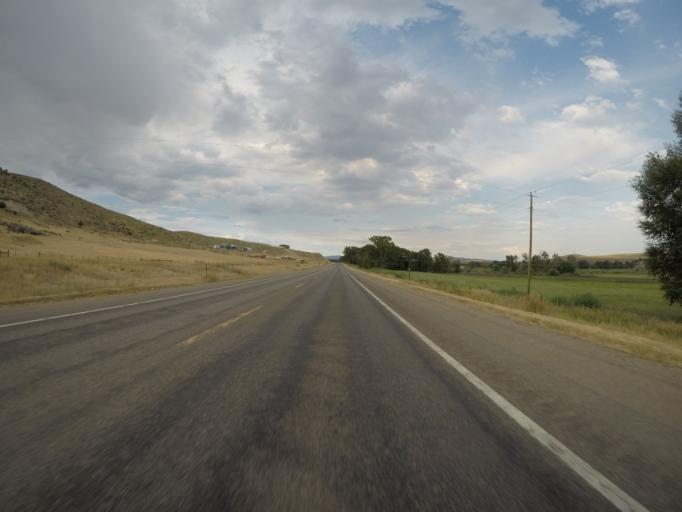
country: US
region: Colorado
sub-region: Moffat County
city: Craig
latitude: 40.5218
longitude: -107.4706
